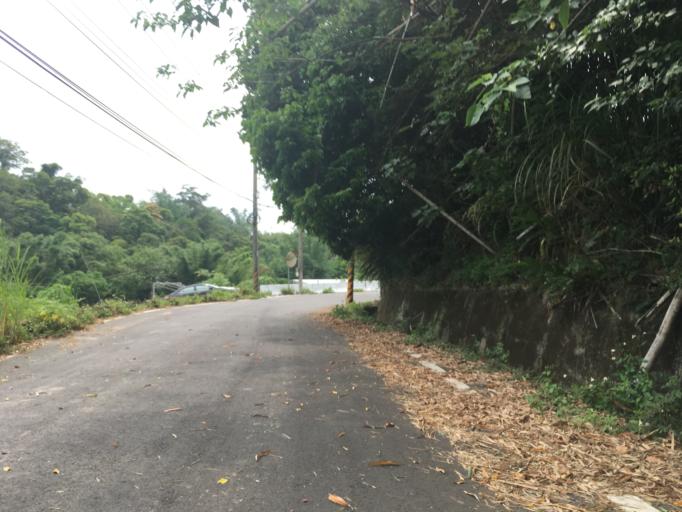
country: TW
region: Taiwan
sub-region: Hsinchu
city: Hsinchu
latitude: 24.7373
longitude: 120.9763
